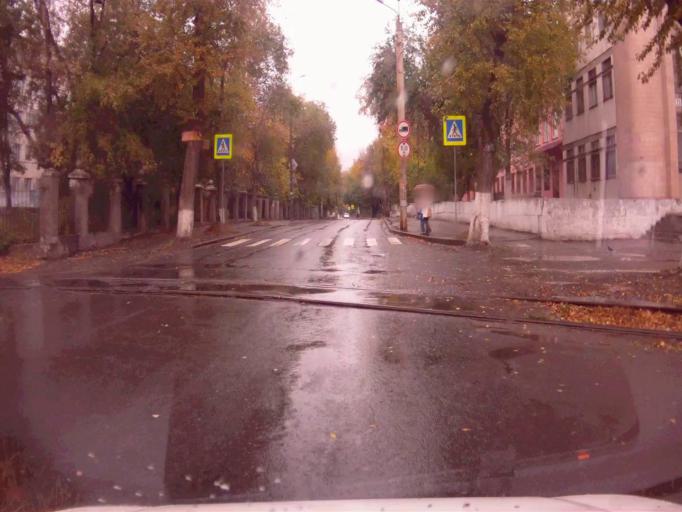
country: RU
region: Chelyabinsk
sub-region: Gorod Chelyabinsk
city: Chelyabinsk
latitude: 55.1913
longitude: 61.4123
